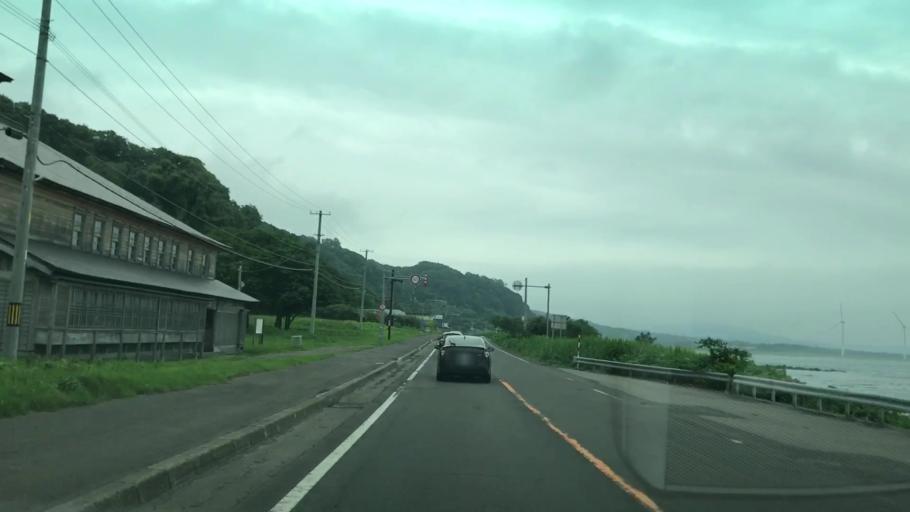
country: JP
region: Hokkaido
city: Iwanai
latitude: 42.7896
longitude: 140.3083
